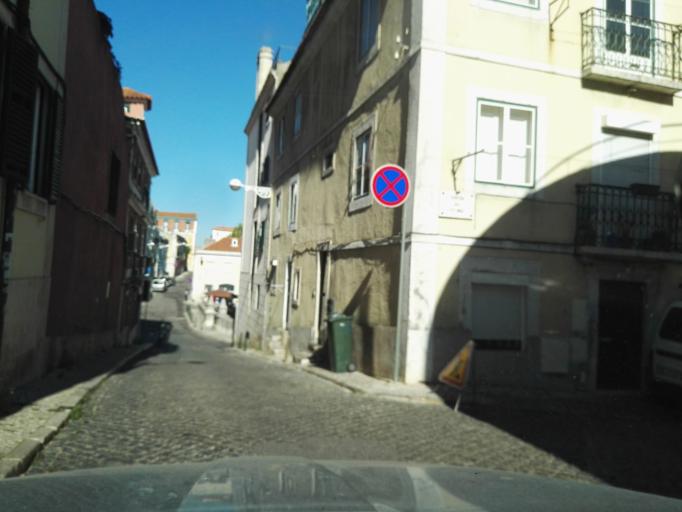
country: PT
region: Setubal
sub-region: Almada
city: Cacilhas
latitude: 38.7045
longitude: -9.1645
